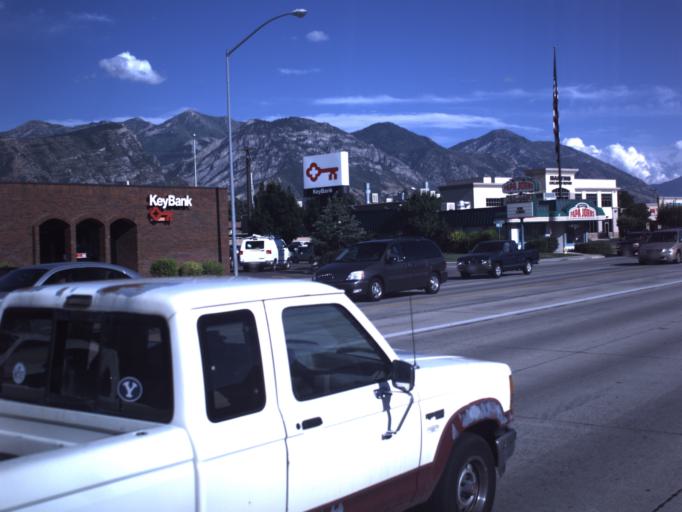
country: US
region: Utah
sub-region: Utah County
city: Orem
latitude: 40.2938
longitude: -111.6937
